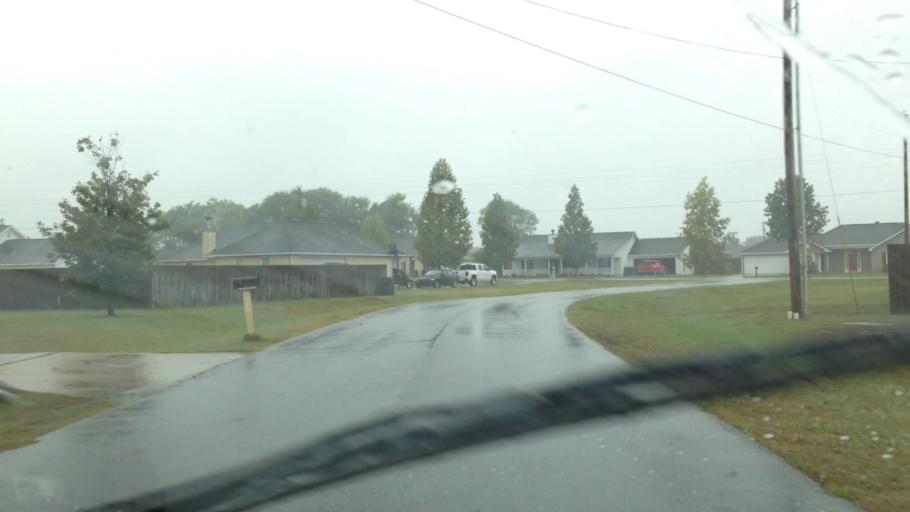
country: US
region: Georgia
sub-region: Muscogee County
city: Columbus
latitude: 32.2644
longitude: -84.9748
